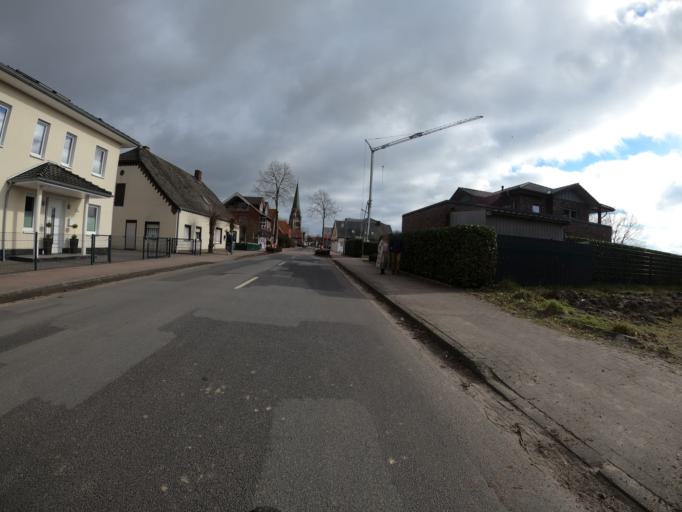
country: DE
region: Lower Saxony
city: Herzlake
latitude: 52.6856
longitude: 7.6001
